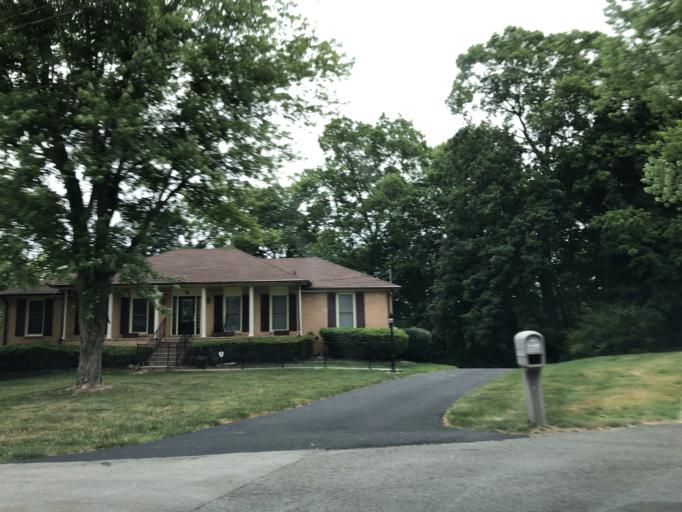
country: US
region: Tennessee
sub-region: Davidson County
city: Goodlettsville
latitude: 36.2799
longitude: -86.7693
